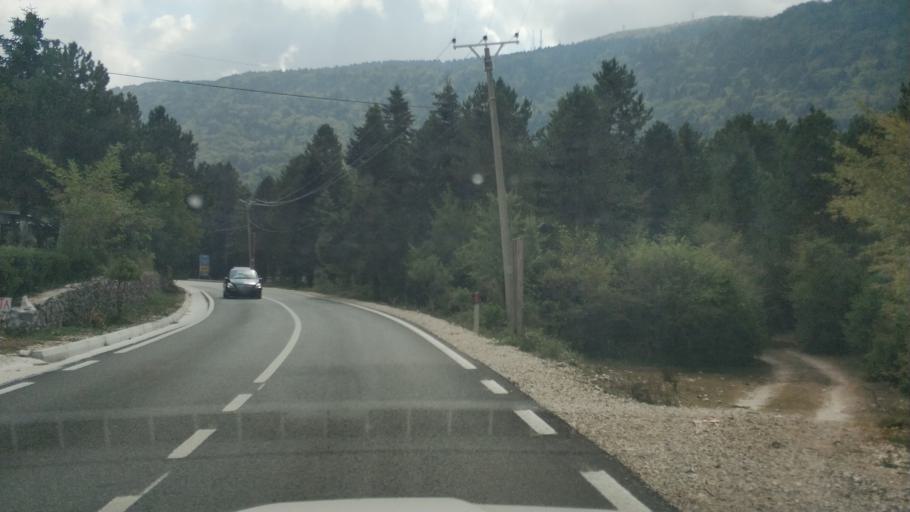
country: AL
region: Vlore
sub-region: Rrethi i Vlores
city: Brataj
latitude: 40.2108
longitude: 19.5791
